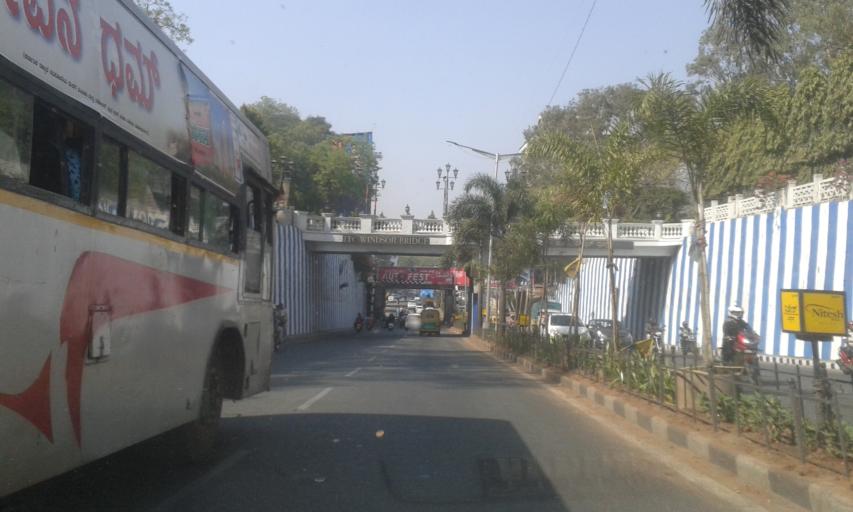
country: IN
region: Karnataka
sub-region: Bangalore Urban
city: Bangalore
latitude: 12.9948
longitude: 77.5850
